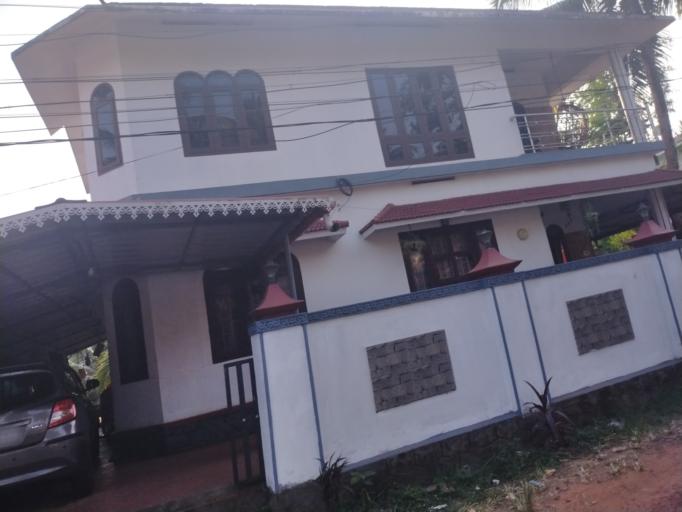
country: IN
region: Kerala
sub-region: Kottayam
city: Vaikam
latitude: 9.7563
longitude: 76.4977
